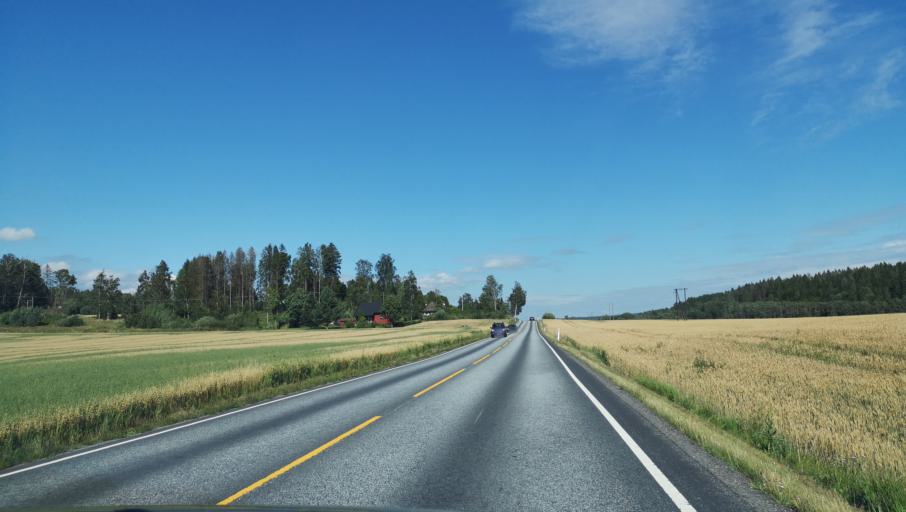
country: NO
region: Ostfold
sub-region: Hobol
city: Elvestad
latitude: 59.5997
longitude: 10.9042
